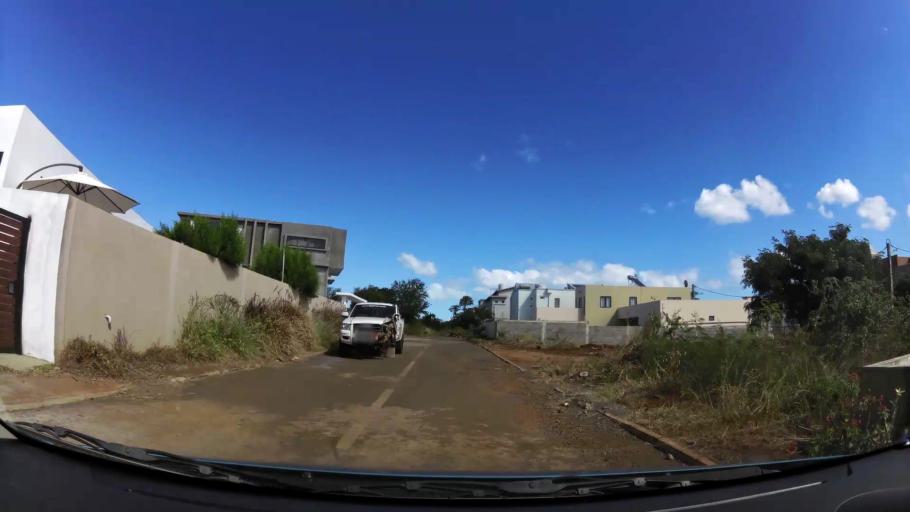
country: MU
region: Black River
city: Albion
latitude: -20.2233
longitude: 57.4163
